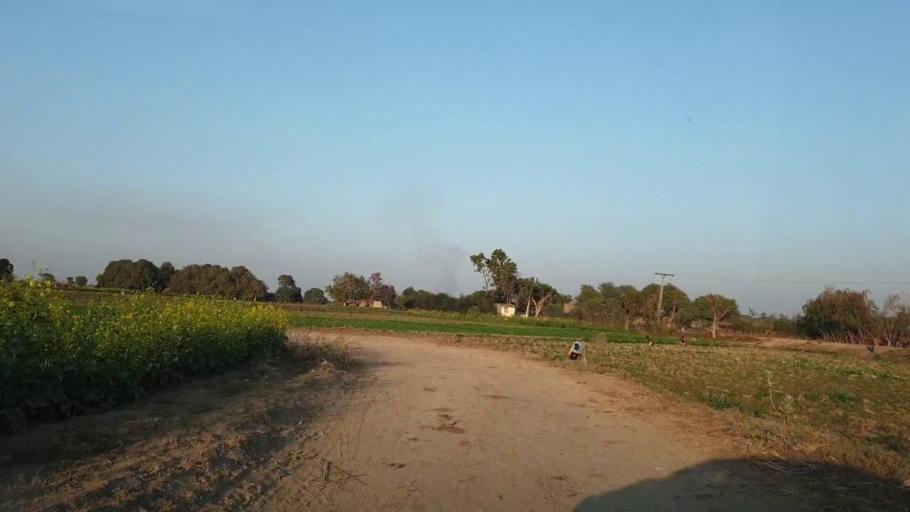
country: PK
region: Sindh
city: Tando Jam
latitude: 25.4829
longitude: 68.6027
